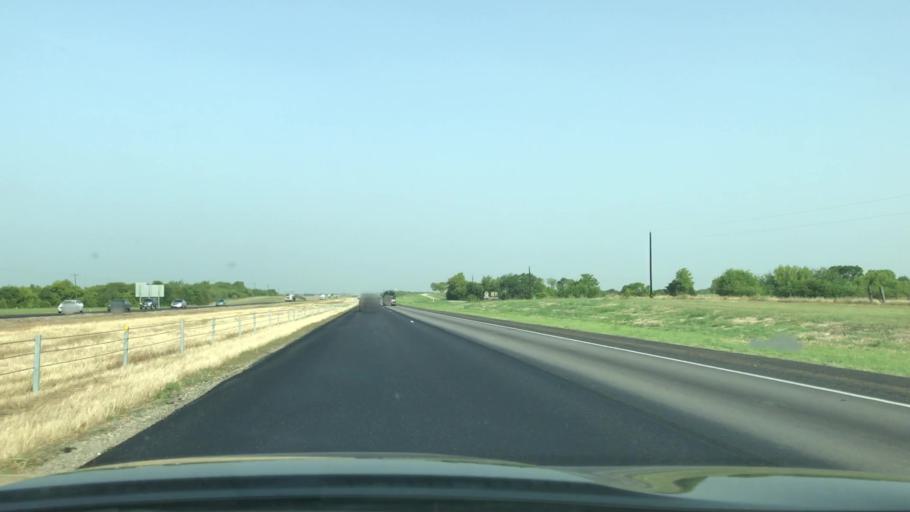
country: US
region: Texas
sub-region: Kaufman County
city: Terrell
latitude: 32.6854
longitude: -96.2113
